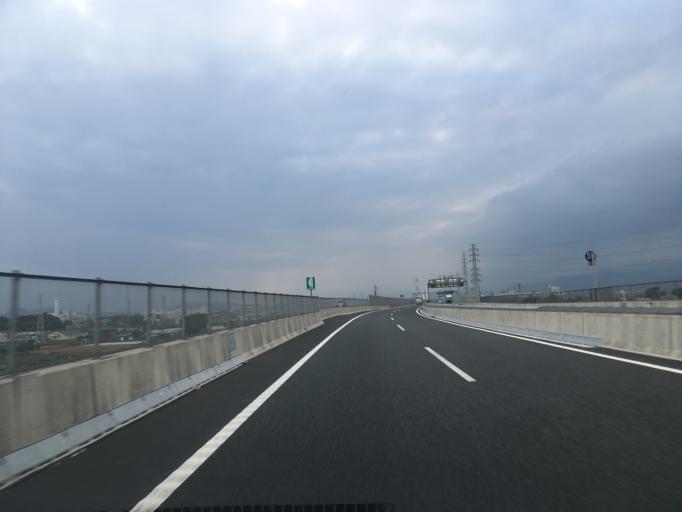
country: JP
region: Kanagawa
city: Chigasaki
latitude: 35.3511
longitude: 139.3882
